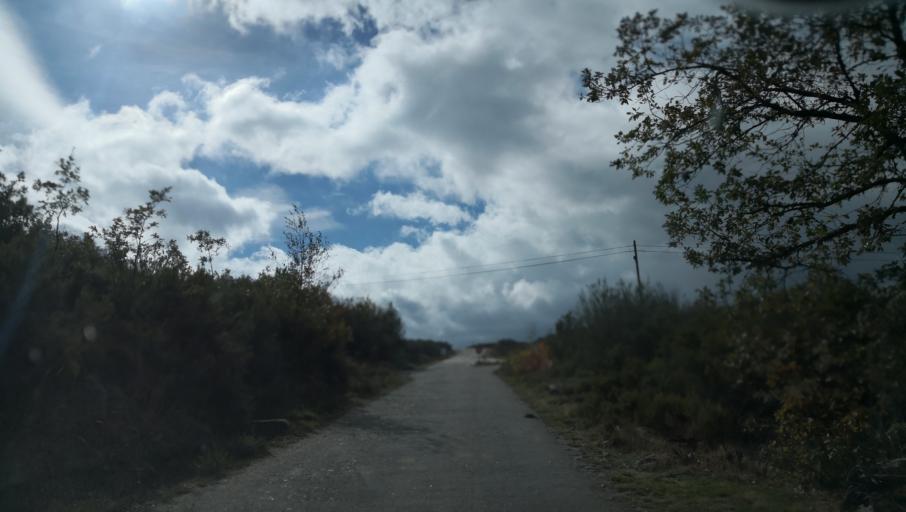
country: PT
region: Vila Real
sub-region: Vila Real
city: Vila Real
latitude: 41.3621
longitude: -7.7948
